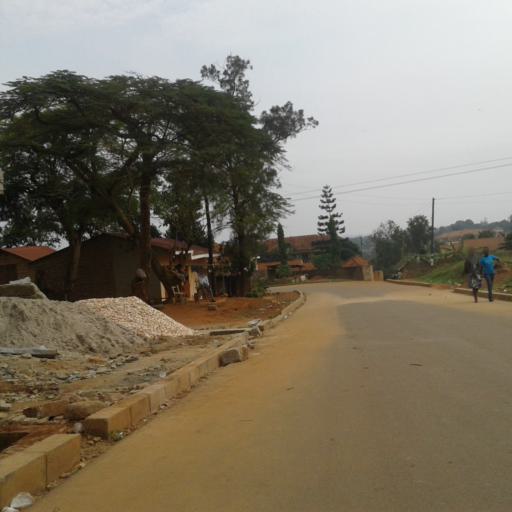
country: UG
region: Central Region
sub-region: Kampala District
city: Kampala
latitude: 0.2667
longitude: 32.6272
